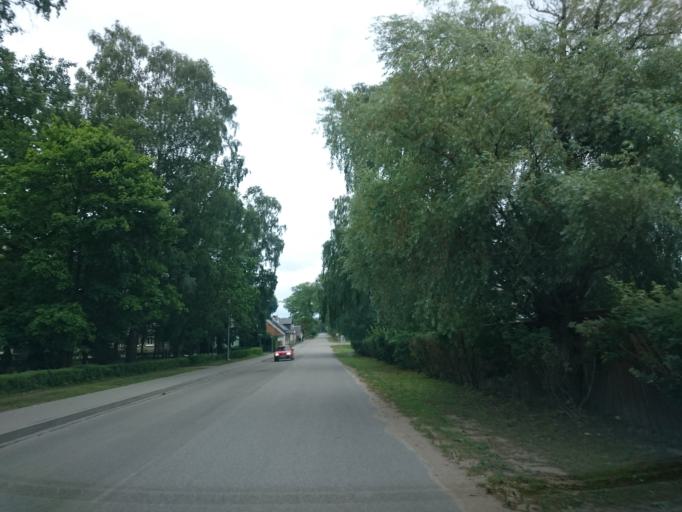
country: LV
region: Pavilostas
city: Pavilosta
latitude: 56.8879
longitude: 21.1819
